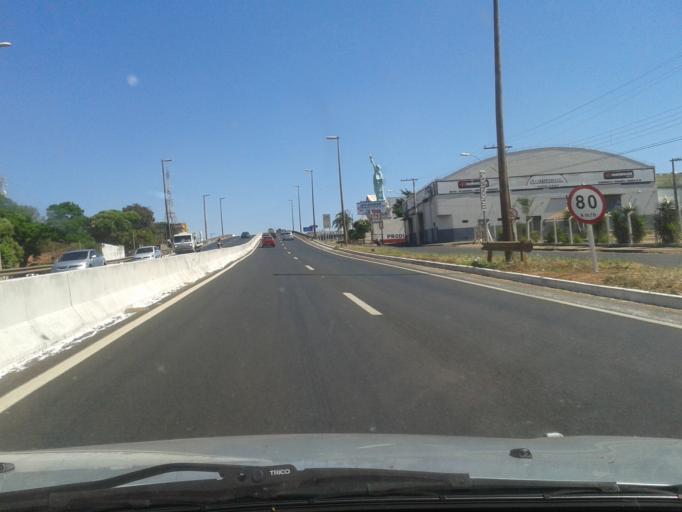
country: BR
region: Minas Gerais
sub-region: Uberlandia
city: Uberlandia
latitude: -18.8921
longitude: -48.2537
